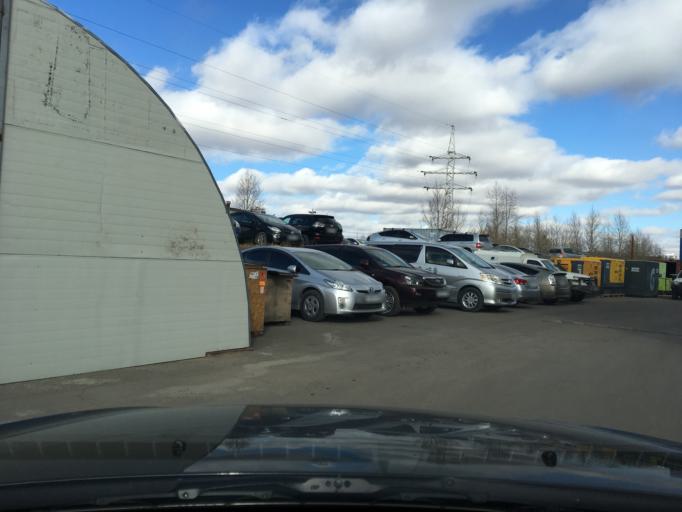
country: MN
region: Ulaanbaatar
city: Ulaanbaatar
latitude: 47.8917
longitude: 106.8685
